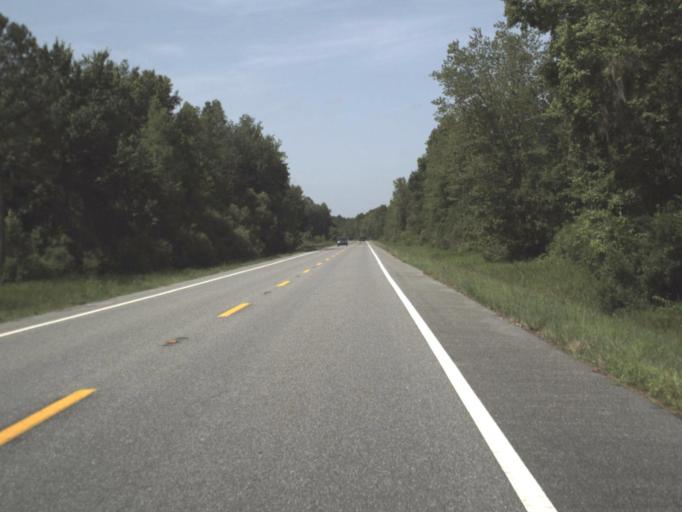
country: US
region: Florida
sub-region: Lafayette County
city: Mayo
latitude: 29.8840
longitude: -83.3037
